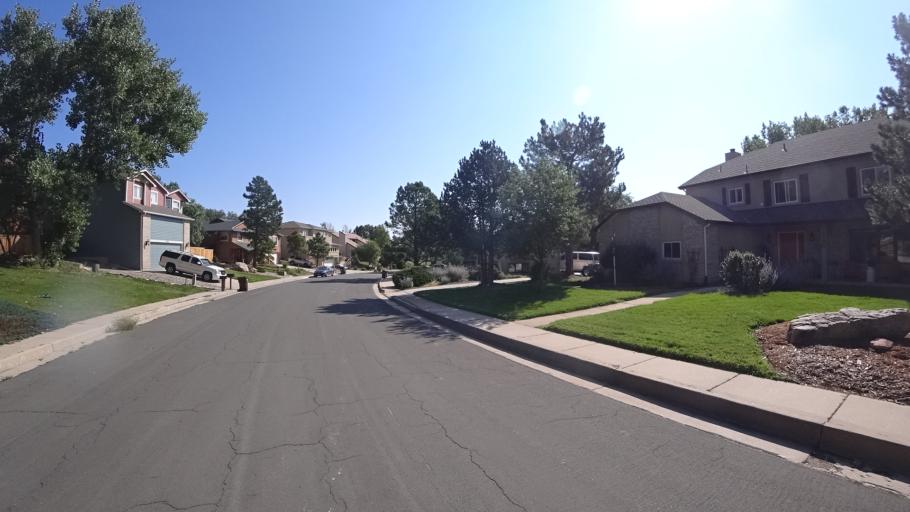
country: US
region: Colorado
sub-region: El Paso County
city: Manitou Springs
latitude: 38.9066
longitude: -104.8753
